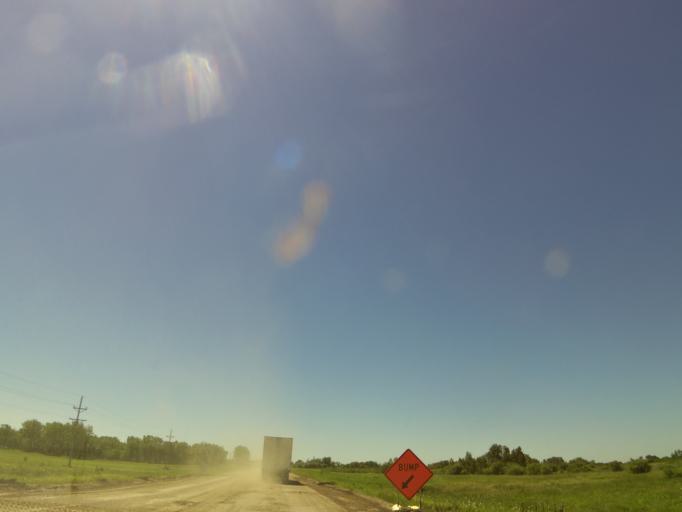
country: US
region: Minnesota
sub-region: Mahnomen County
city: Mahnomen
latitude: 47.1201
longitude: -95.9270
